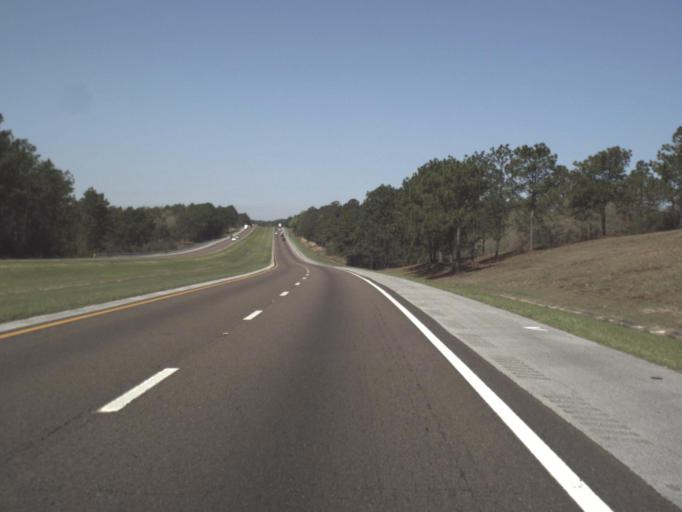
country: US
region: Florida
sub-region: Walton County
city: DeFuniak Springs
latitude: 30.7223
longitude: -86.1869
